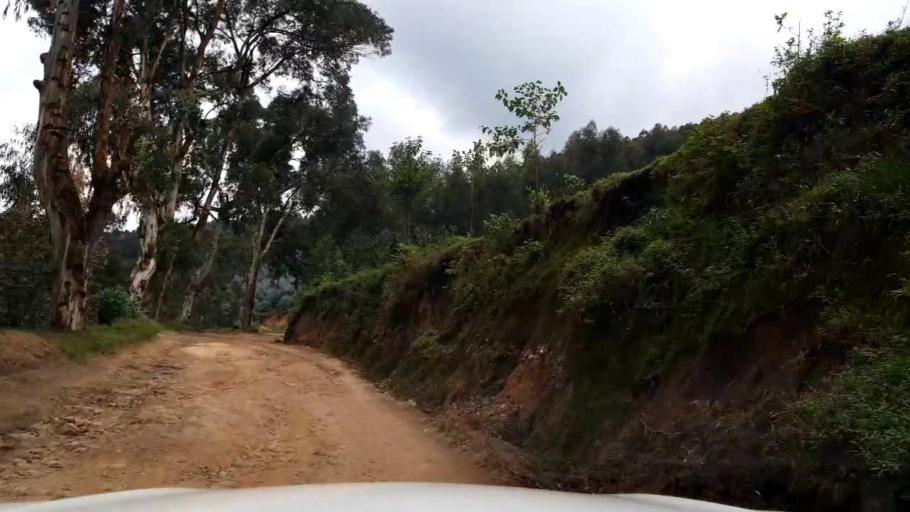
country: RW
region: Western Province
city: Kibuye
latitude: -1.9612
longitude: 29.3944
